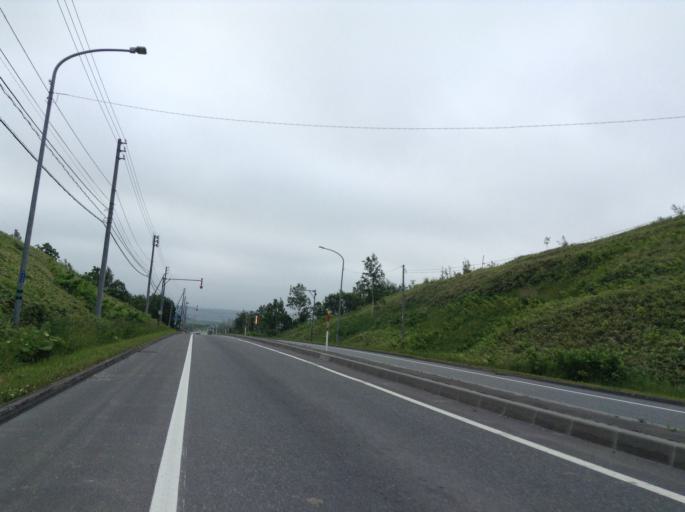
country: JP
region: Hokkaido
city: Wakkanai
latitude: 45.3734
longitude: 141.7171
